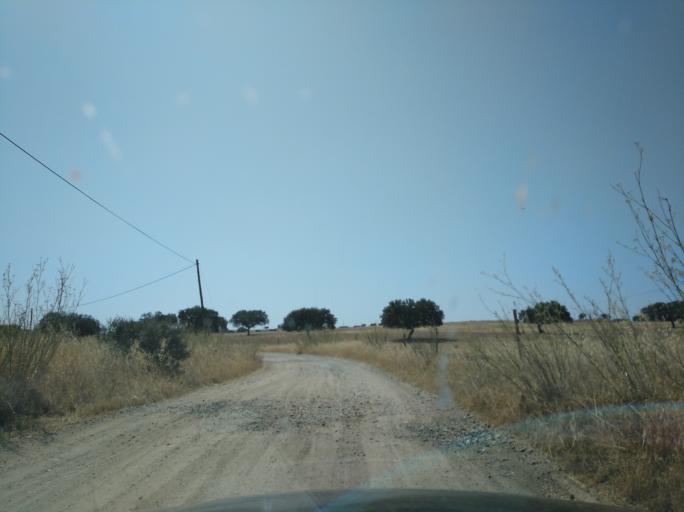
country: PT
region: Portalegre
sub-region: Campo Maior
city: Campo Maior
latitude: 39.0331
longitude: -6.9834
